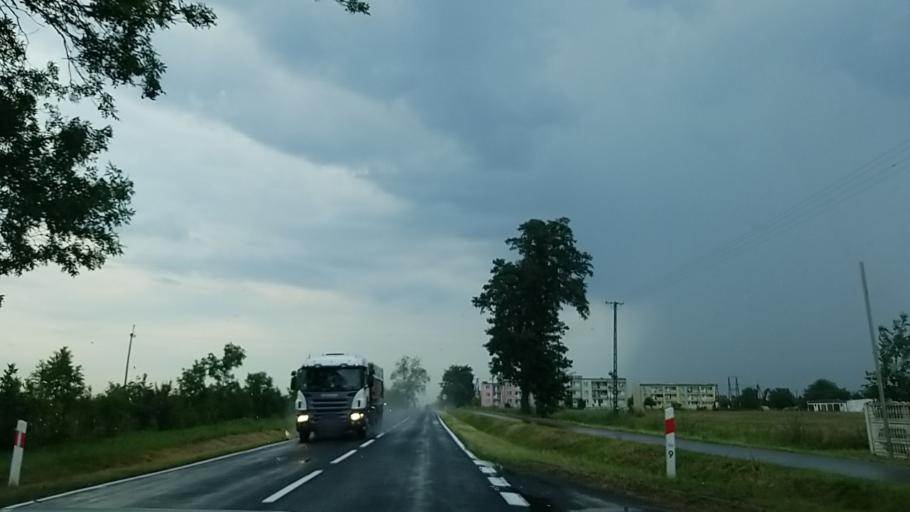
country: PL
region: Lublin Voivodeship
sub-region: Powiat wlodawski
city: Wlodawa
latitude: 51.6124
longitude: 23.5295
